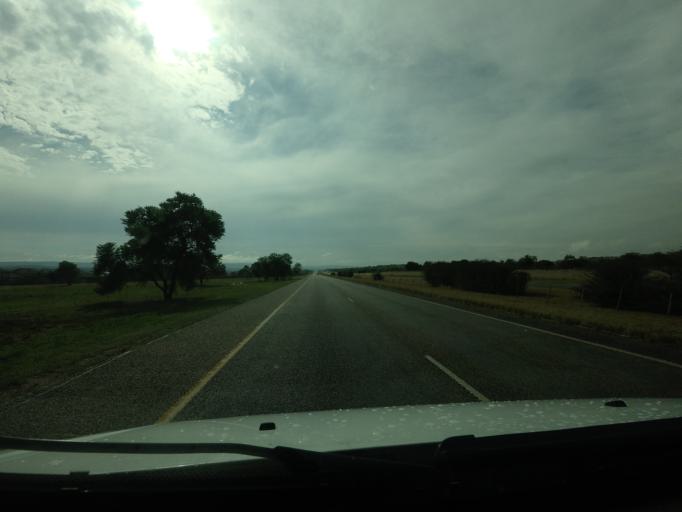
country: ZA
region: Gauteng
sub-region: City of Tshwane Metropolitan Municipality
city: Pretoria
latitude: -25.7605
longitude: 28.3657
